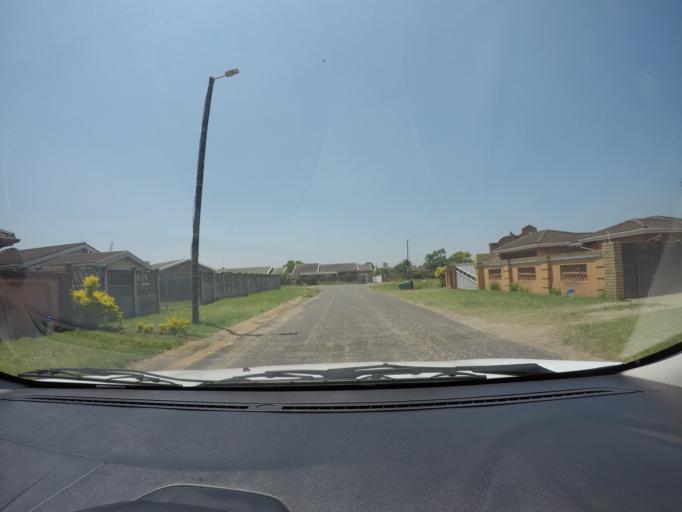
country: ZA
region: KwaZulu-Natal
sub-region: uThungulu District Municipality
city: eSikhawini
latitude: -28.8890
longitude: 31.8844
